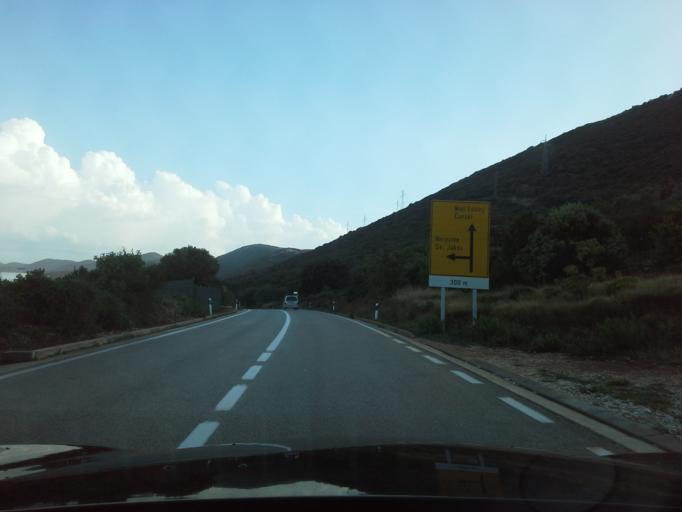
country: HR
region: Primorsko-Goranska
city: Mali Losinj
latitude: 44.6410
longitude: 14.3907
